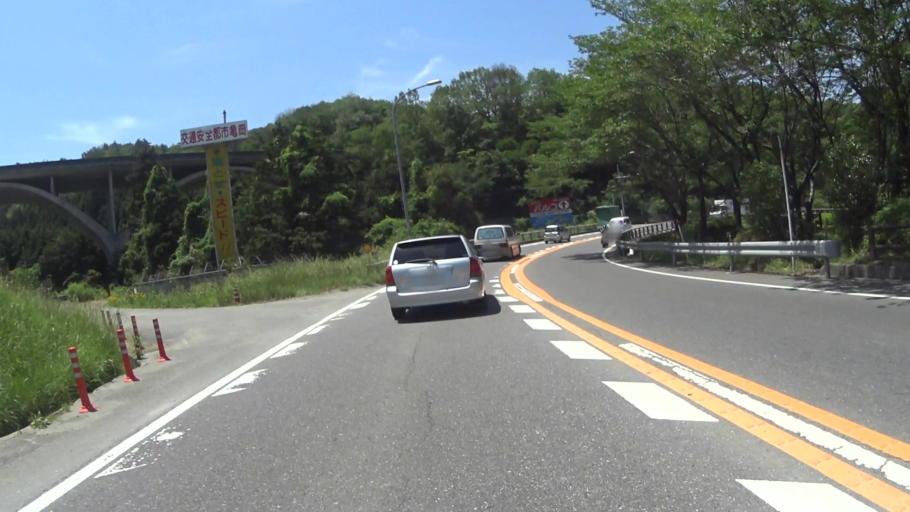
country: JP
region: Kyoto
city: Kameoka
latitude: 34.9908
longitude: 135.6257
